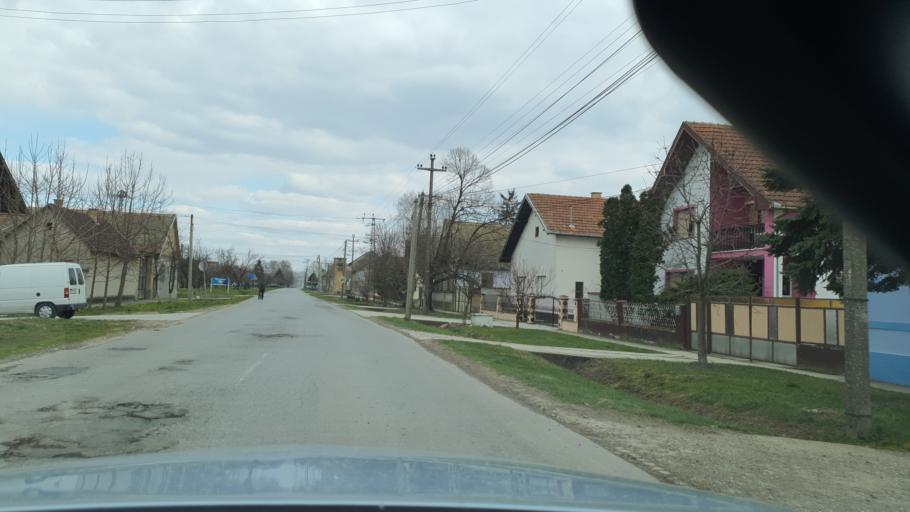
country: RS
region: Autonomna Pokrajina Vojvodina
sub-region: Juznobacki Okrug
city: Bac
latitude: 45.4119
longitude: 19.3059
